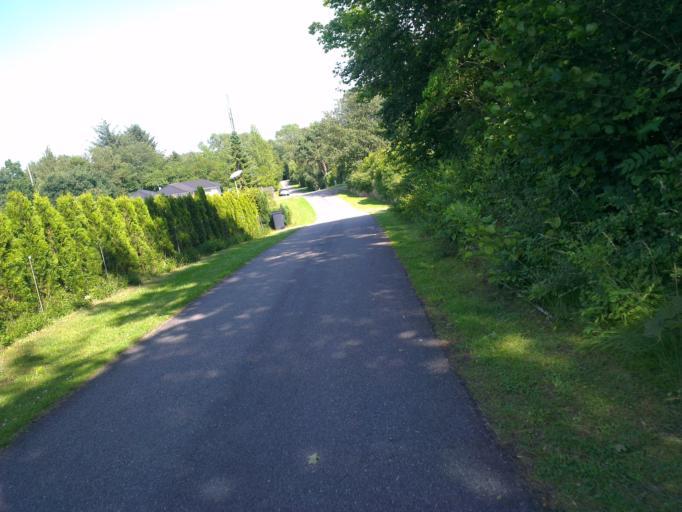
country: DK
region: Capital Region
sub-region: Halsnaes Kommune
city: Hundested
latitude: 55.9233
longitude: 11.9178
